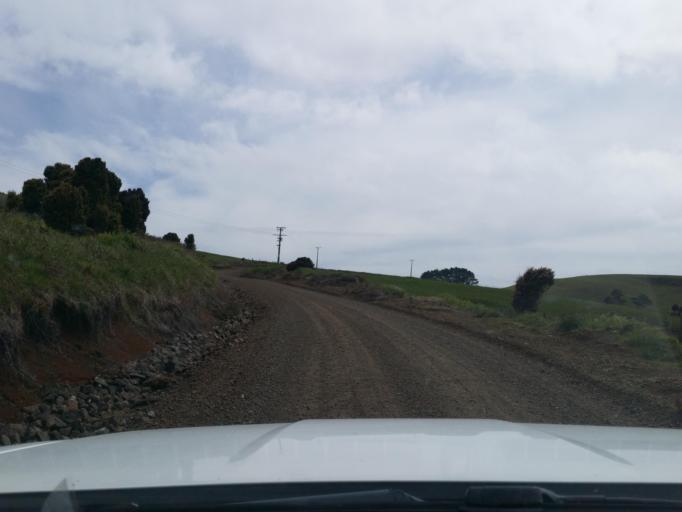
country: NZ
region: Northland
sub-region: Kaipara District
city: Dargaville
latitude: -35.7314
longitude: 173.5756
